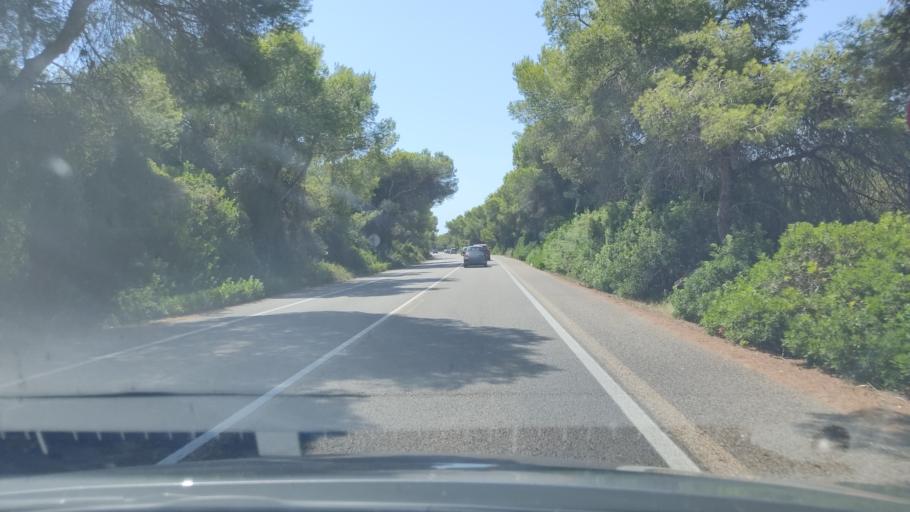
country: ES
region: Valencia
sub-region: Provincia de Valencia
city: Sollana
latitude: 39.3292
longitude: -0.3119
